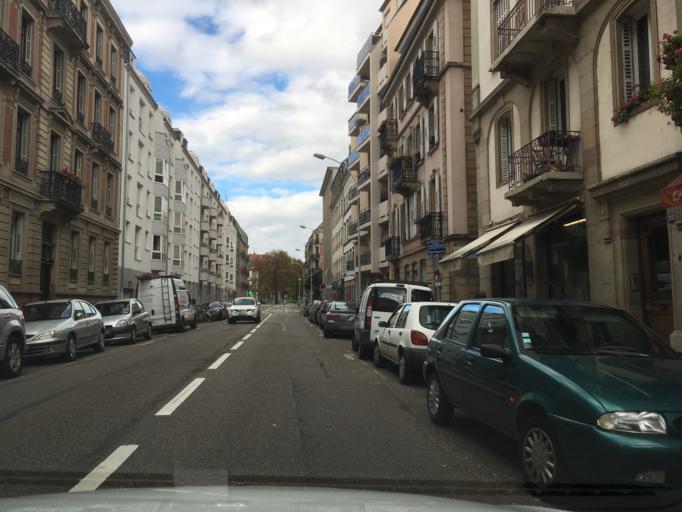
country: FR
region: Alsace
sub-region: Departement du Bas-Rhin
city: Strasbourg
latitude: 48.5803
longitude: 7.7565
